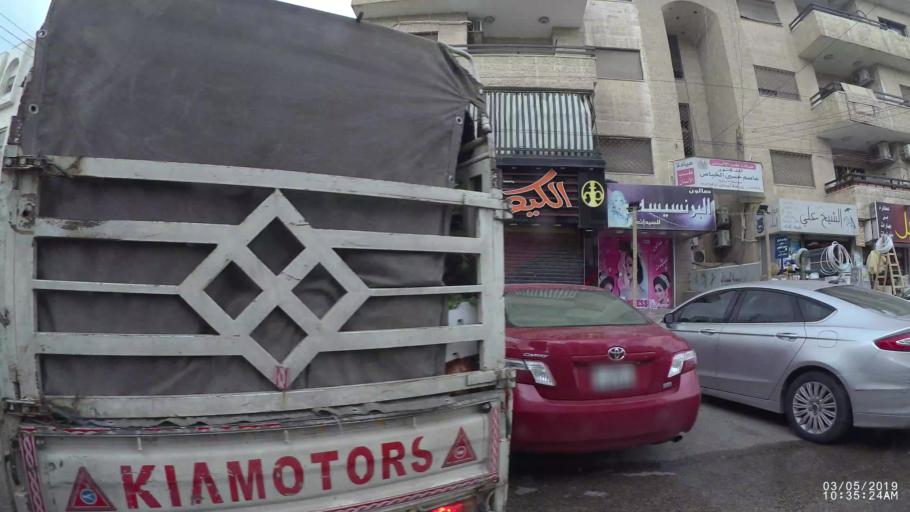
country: JO
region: Amman
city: Amman
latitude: 31.9853
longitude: 35.9240
